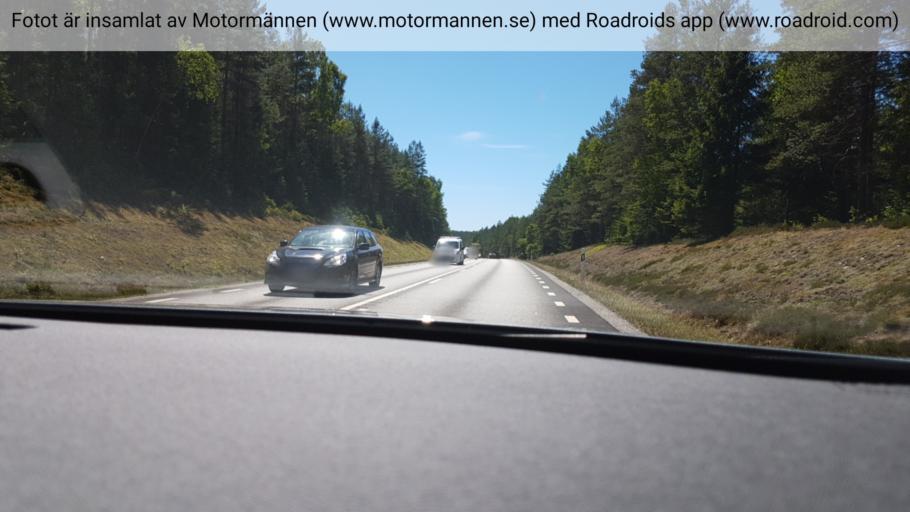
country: SE
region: Joenkoeping
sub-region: Gnosjo Kommun
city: Gnosjoe
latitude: 57.5663
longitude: 13.7024
